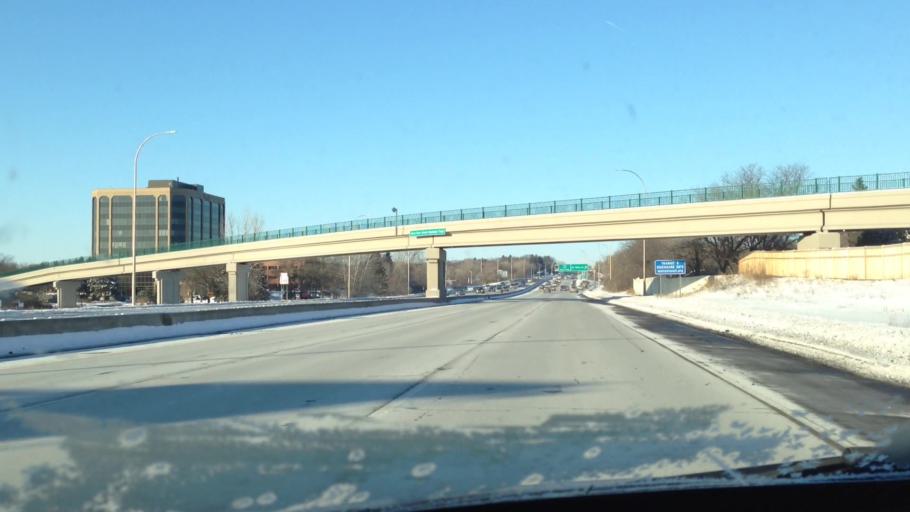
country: US
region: Minnesota
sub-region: Hennepin County
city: Edina
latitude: 44.8706
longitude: -93.3502
